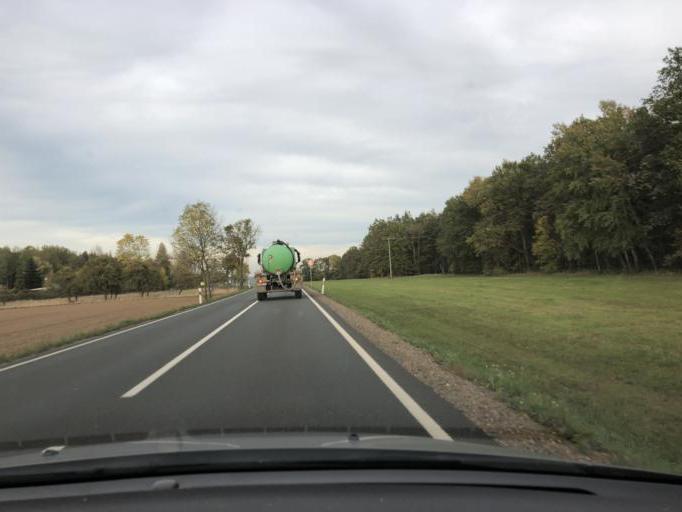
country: DE
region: Thuringia
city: Zedlitz
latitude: 50.8267
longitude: 12.0120
